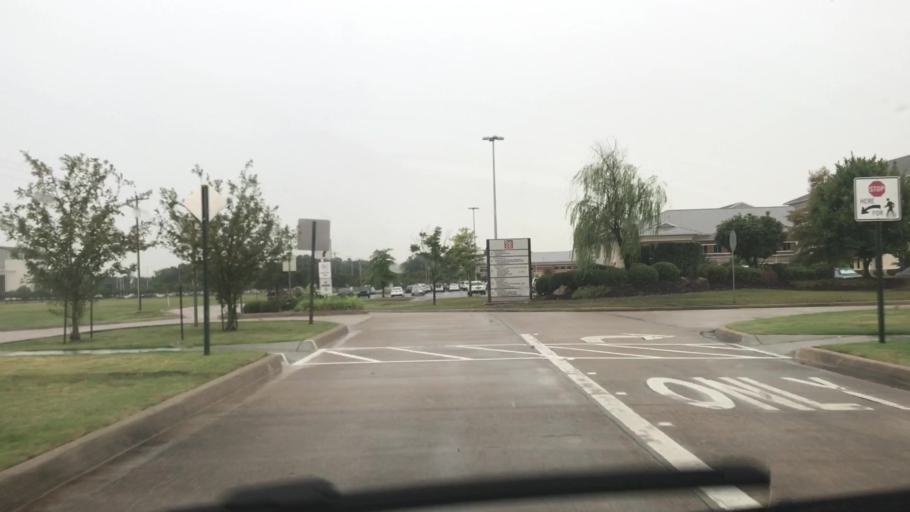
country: US
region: Louisiana
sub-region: Bossier Parish
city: Red Chute
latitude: 32.5409
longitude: -93.6458
